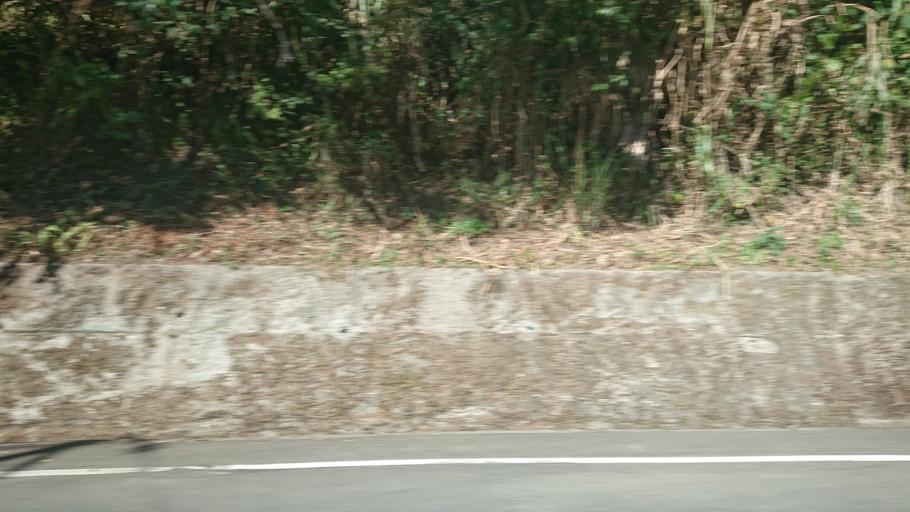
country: TW
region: Taiwan
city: Lugu
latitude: 23.4894
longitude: 120.7609
